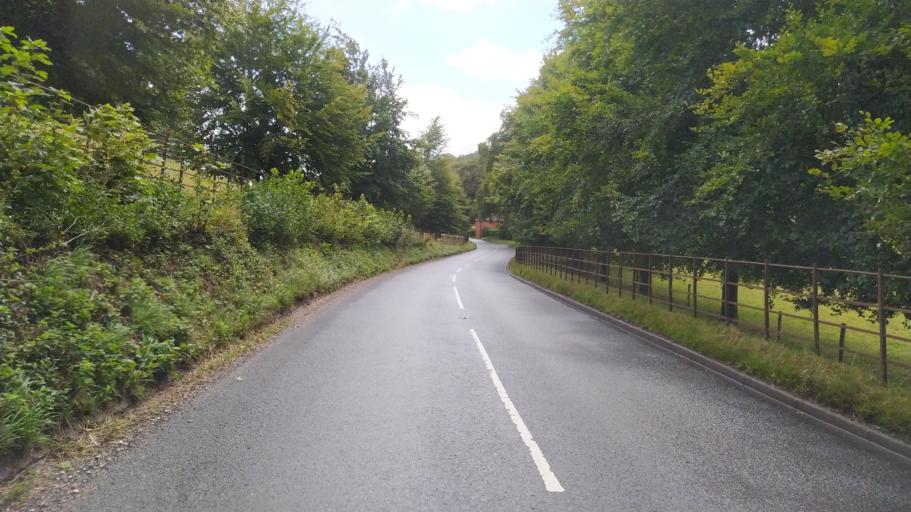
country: GB
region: England
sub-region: Wiltshire
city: Ansty
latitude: 50.9538
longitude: -2.0737
